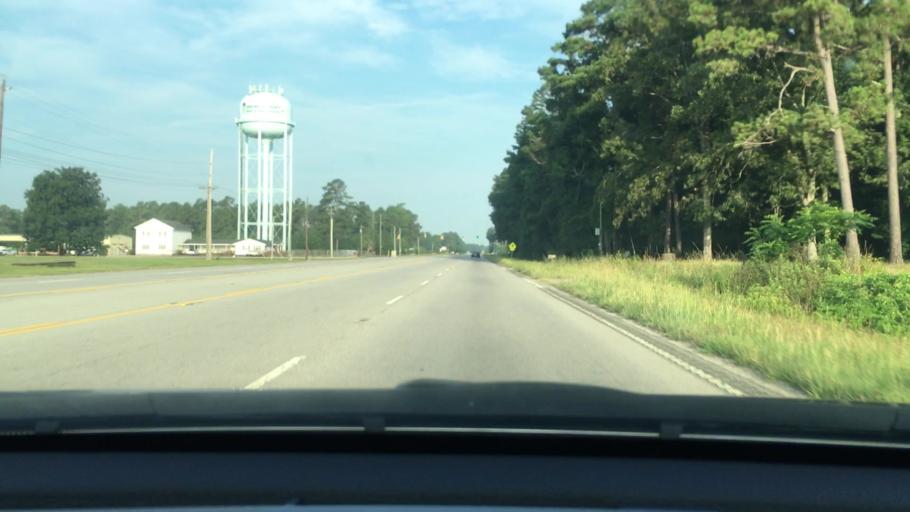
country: US
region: South Carolina
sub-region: Darlington County
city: Darlington
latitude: 34.2999
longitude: -79.9279
